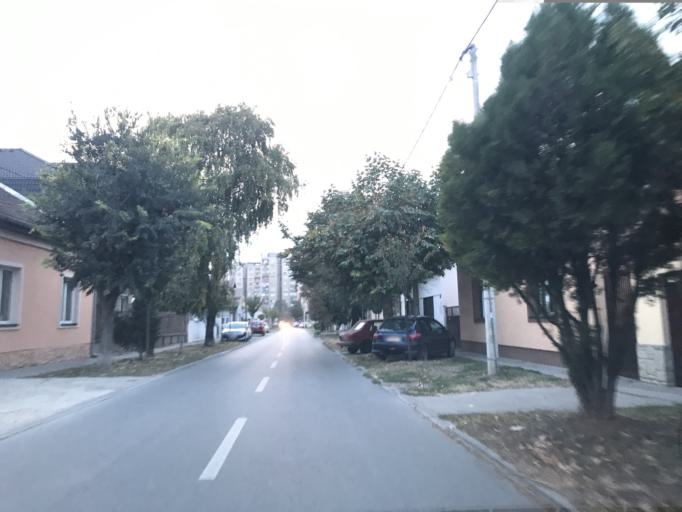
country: RS
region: Autonomna Pokrajina Vojvodina
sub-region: Juznobacki Okrug
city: Novi Sad
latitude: 45.2663
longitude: 19.8392
